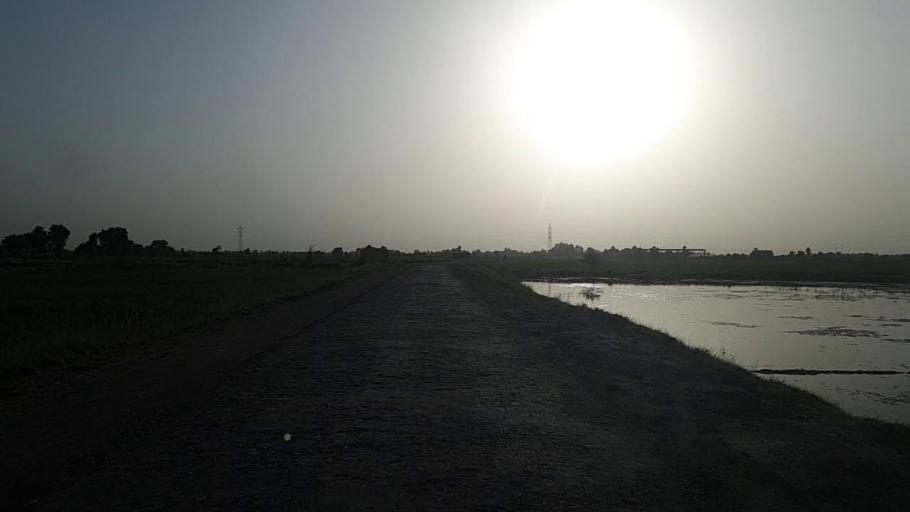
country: PK
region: Sindh
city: Naushahro Firoz
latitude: 26.8086
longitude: 68.1098
